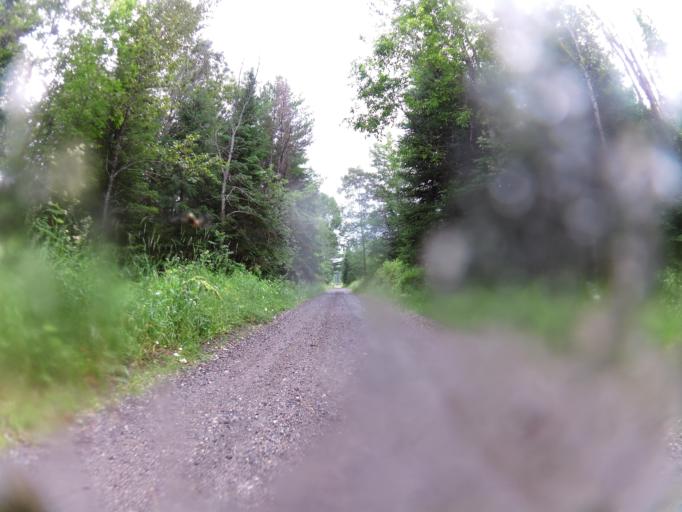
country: CA
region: Ontario
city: Renfrew
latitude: 45.0775
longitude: -76.7206
